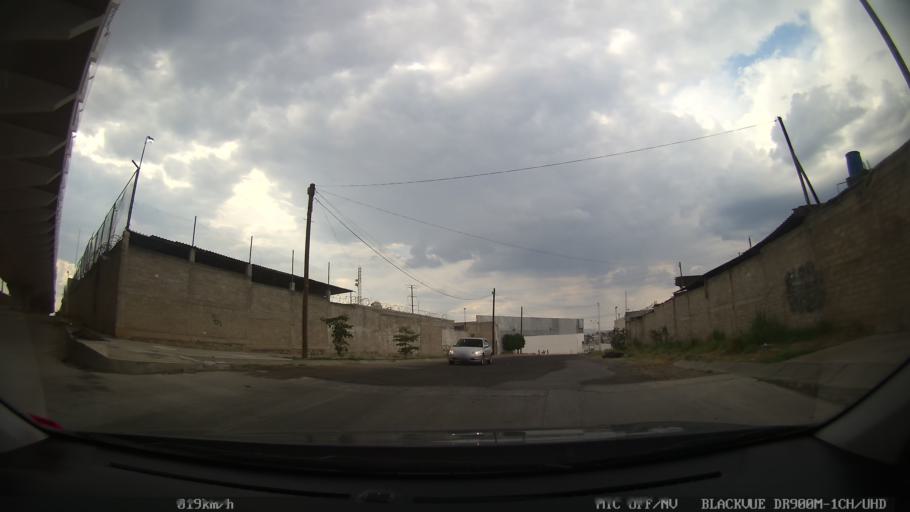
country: MX
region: Jalisco
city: Tlaquepaque
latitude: 20.6215
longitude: -103.2793
